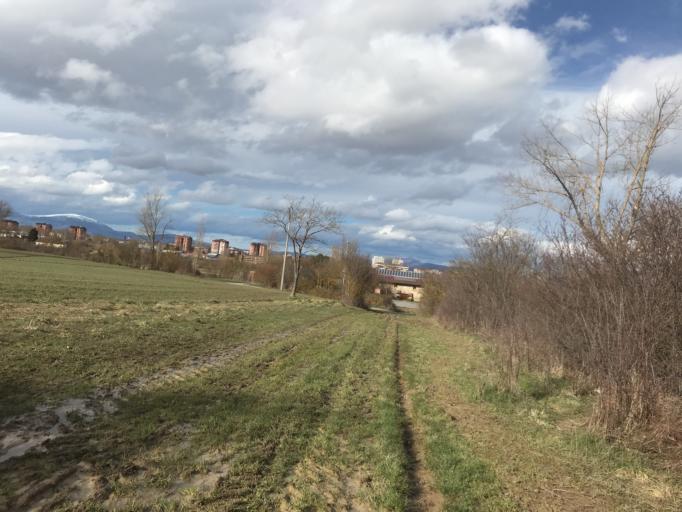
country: ES
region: Basque Country
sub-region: Provincia de Alava
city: Gasteiz / Vitoria
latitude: 42.8238
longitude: -2.6610
